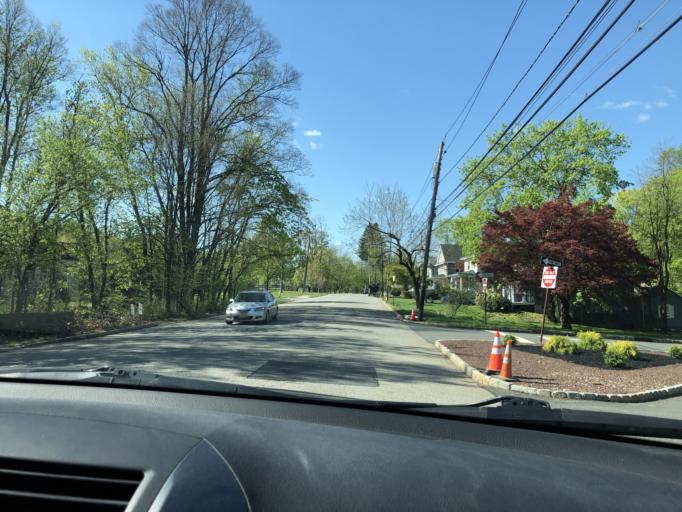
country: US
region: New Jersey
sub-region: Essex County
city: Caldwell
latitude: 40.8465
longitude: -74.2600
